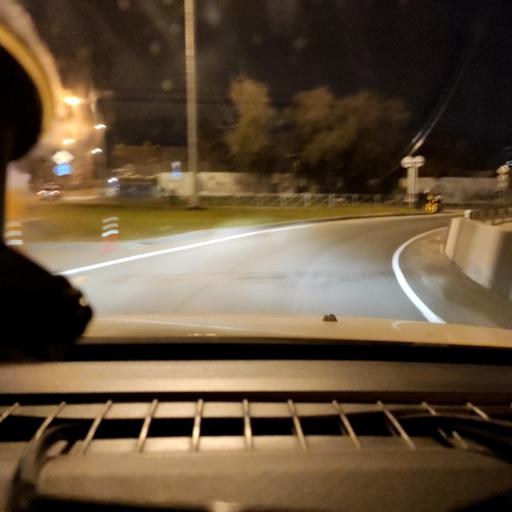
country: RU
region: Samara
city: Rozhdestveno
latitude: 53.1783
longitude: 50.0857
